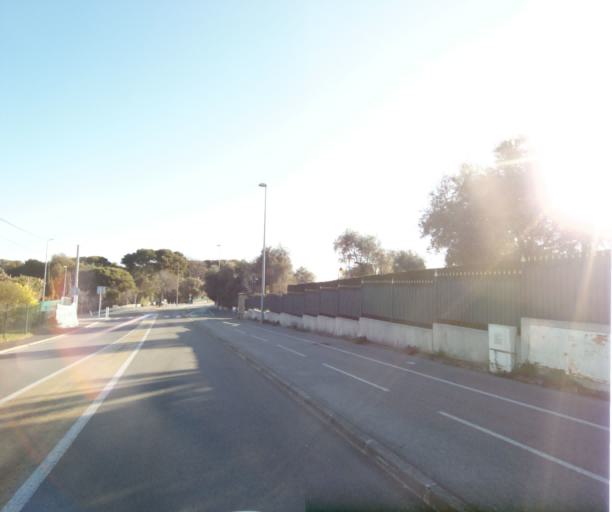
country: FR
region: Provence-Alpes-Cote d'Azur
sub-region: Departement des Alpes-Maritimes
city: Vallauris
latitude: 43.5959
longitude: 7.0831
